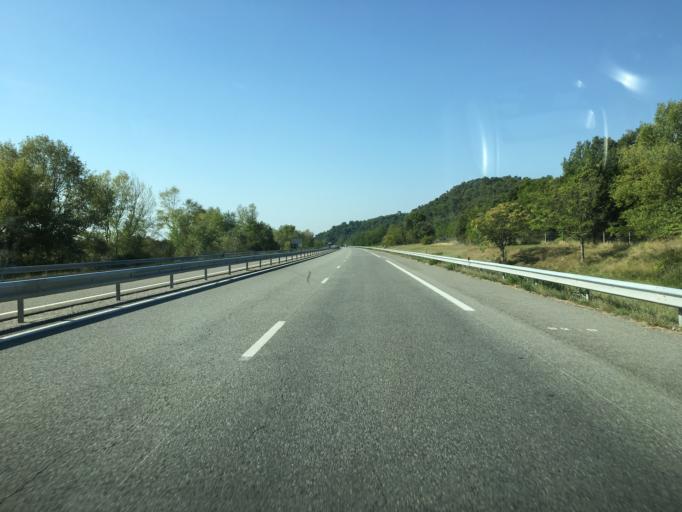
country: FR
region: Provence-Alpes-Cote d'Azur
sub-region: Departement des Alpes-de-Haute-Provence
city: Peyruis
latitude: 43.9903
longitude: 5.9153
